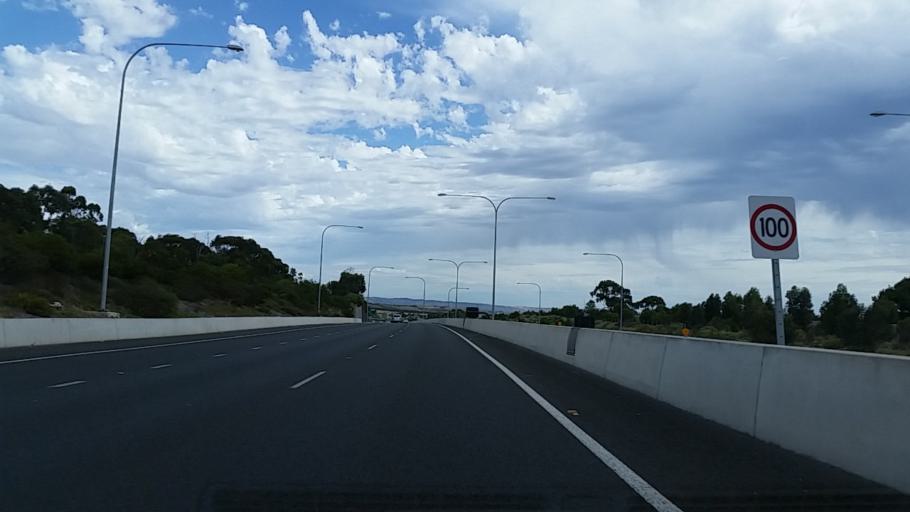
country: AU
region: South Australia
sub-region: Onkaparinga
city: Noarlunga Downs
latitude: -35.1416
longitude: 138.5055
